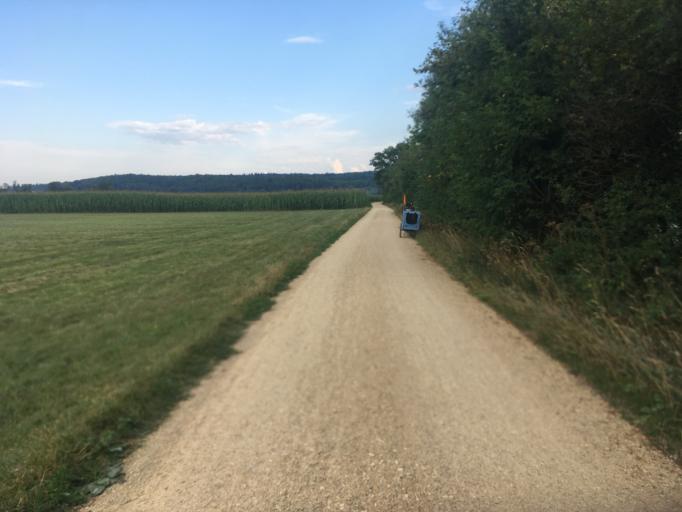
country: CH
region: Solothurn
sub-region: Bezirk Lebern
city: Langendorf
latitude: 47.2031
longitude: 7.4972
